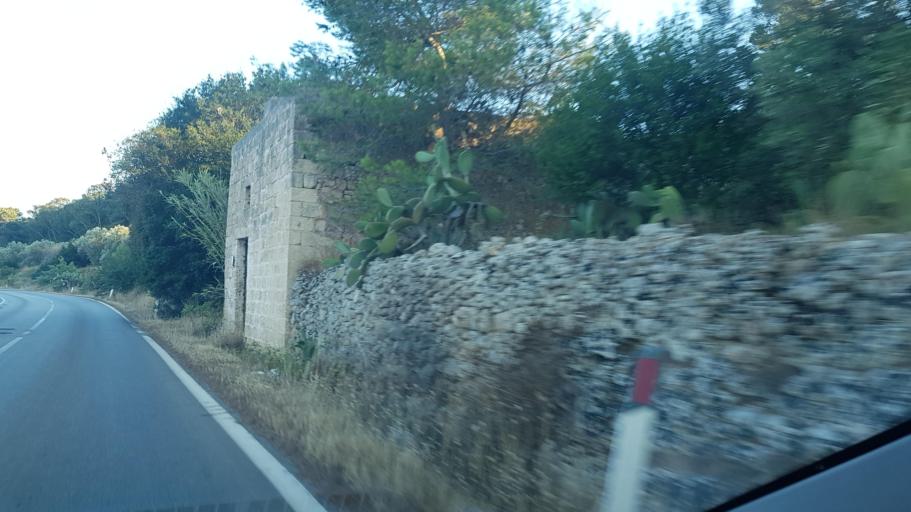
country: IT
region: Apulia
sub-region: Provincia di Lecce
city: Specchia
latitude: 39.9528
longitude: 18.2885
